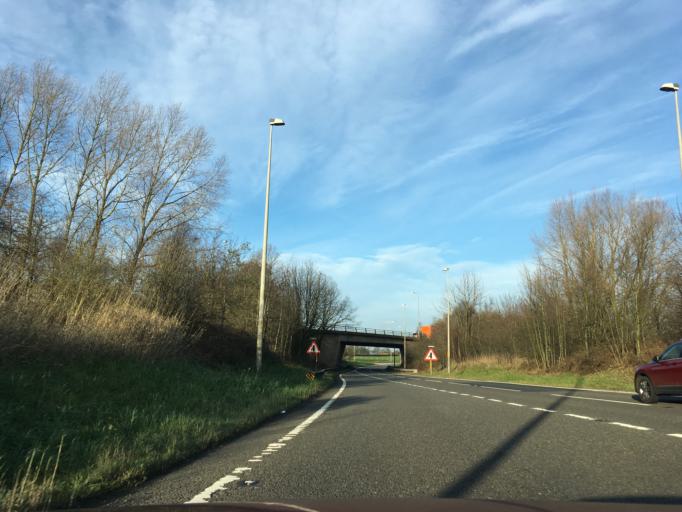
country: GB
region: England
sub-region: Warrington
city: Lymm
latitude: 53.3537
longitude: -2.5057
